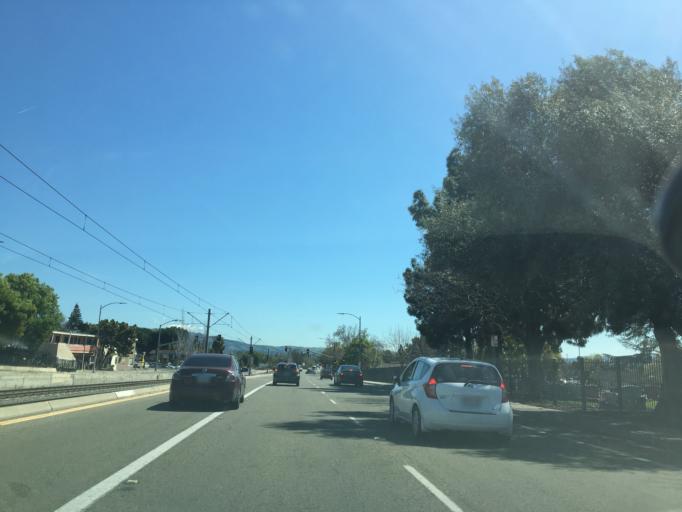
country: US
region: California
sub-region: Santa Clara County
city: Alum Rock
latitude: 37.3634
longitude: -121.8366
